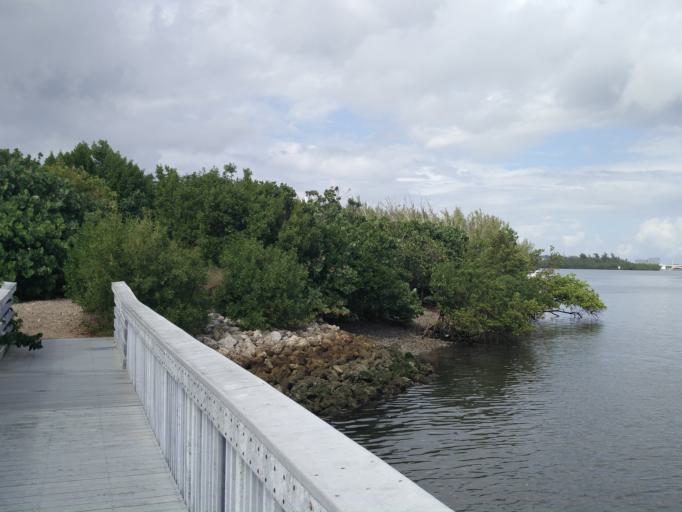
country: US
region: Florida
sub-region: Broward County
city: Dania Beach
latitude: 26.0400
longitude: -80.1176
